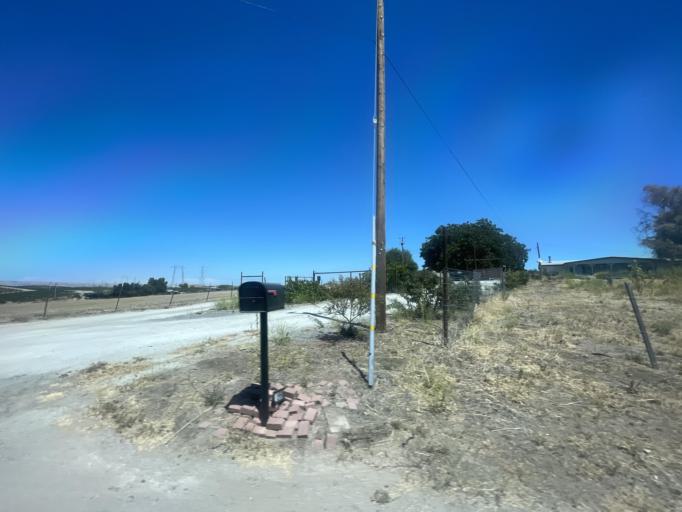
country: US
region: California
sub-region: San Luis Obispo County
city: Paso Robles
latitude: 35.6285
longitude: -120.6143
